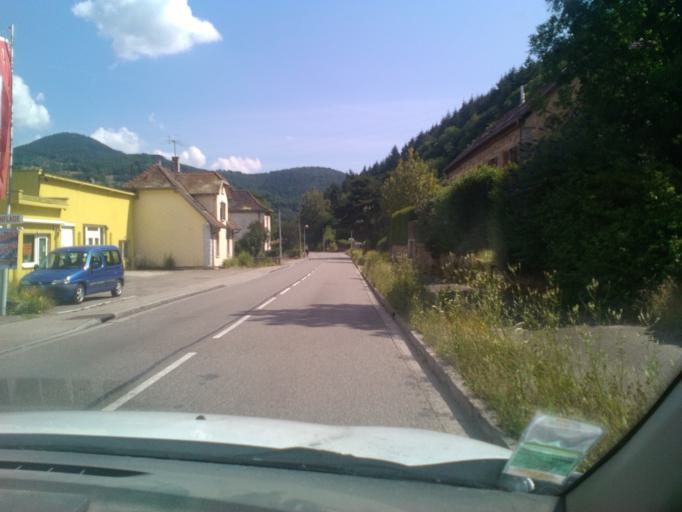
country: FR
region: Alsace
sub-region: Departement du Haut-Rhin
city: Freland
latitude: 48.1494
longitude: 7.1943
